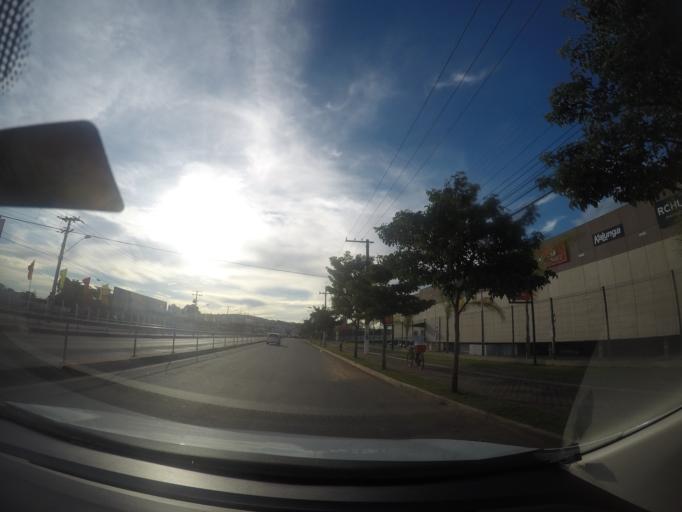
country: BR
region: Goias
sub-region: Goiania
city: Goiania
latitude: -16.6671
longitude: -49.3088
